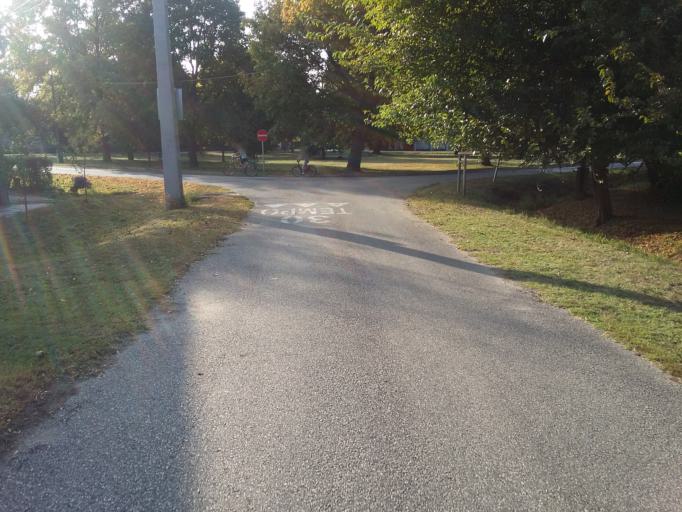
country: HU
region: Csongrad
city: Szeged
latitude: 46.2051
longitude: 20.1108
